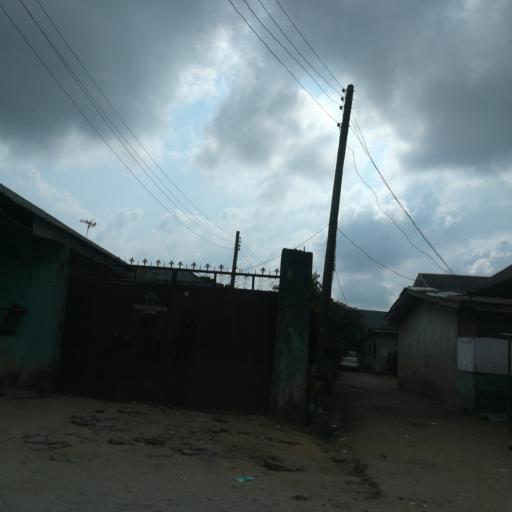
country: NG
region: Rivers
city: Okrika
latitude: 4.7999
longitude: 7.1235
